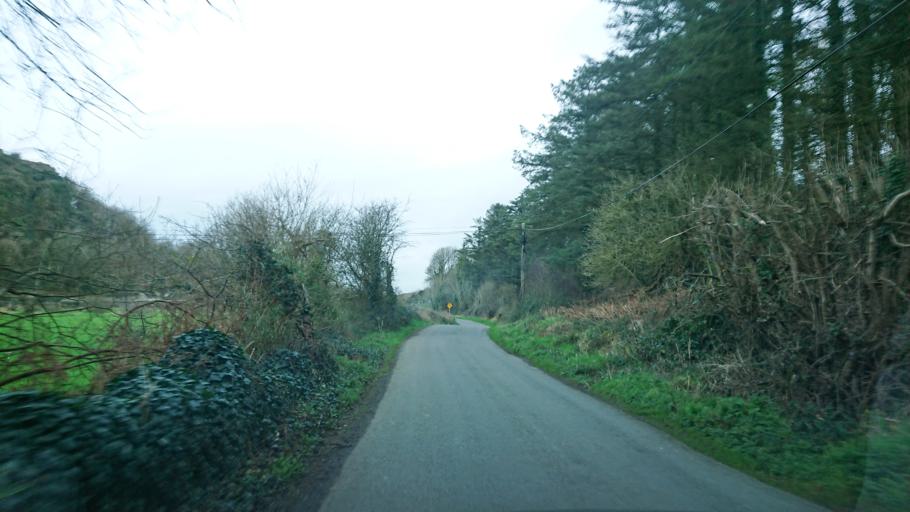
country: IE
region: Munster
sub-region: Waterford
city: Tra Mhor
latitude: 52.1558
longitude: -7.2617
